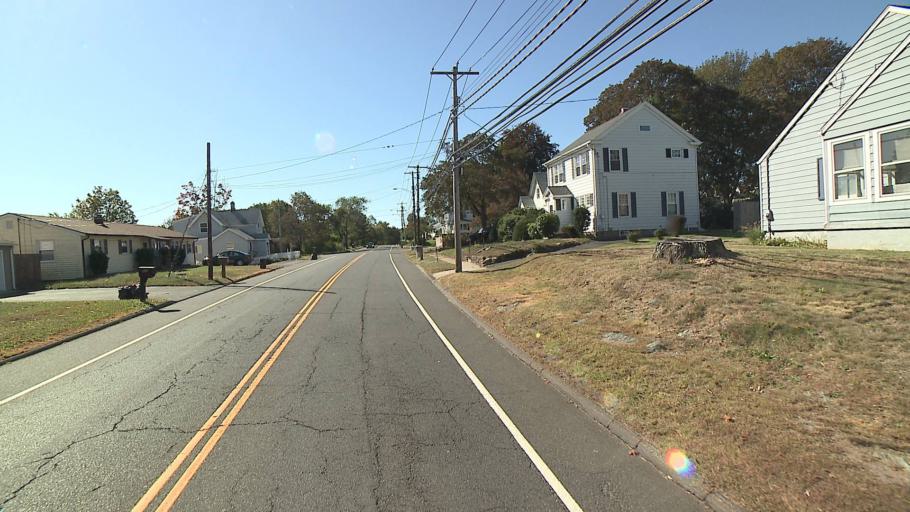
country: US
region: Connecticut
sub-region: New Haven County
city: West Haven
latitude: 41.2671
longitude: -72.9620
